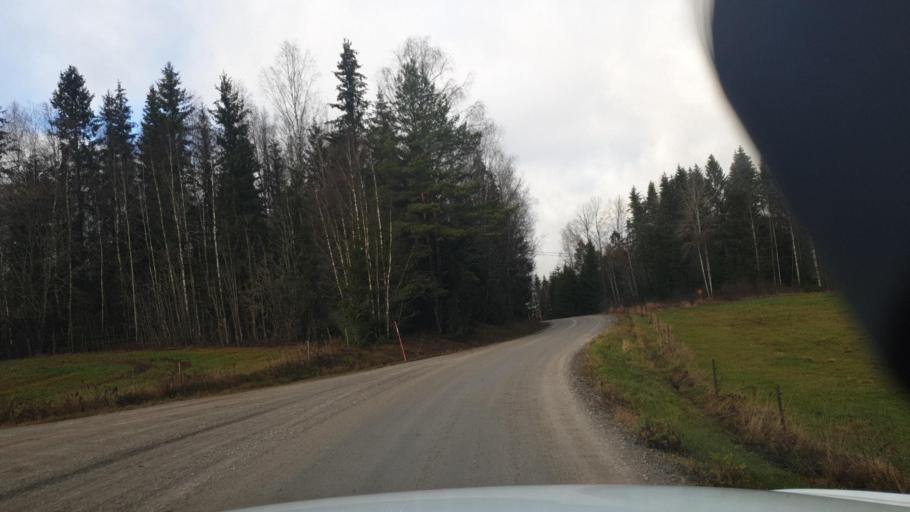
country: SE
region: Vaermland
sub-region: Sunne Kommun
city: Sunne
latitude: 59.6841
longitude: 12.8928
